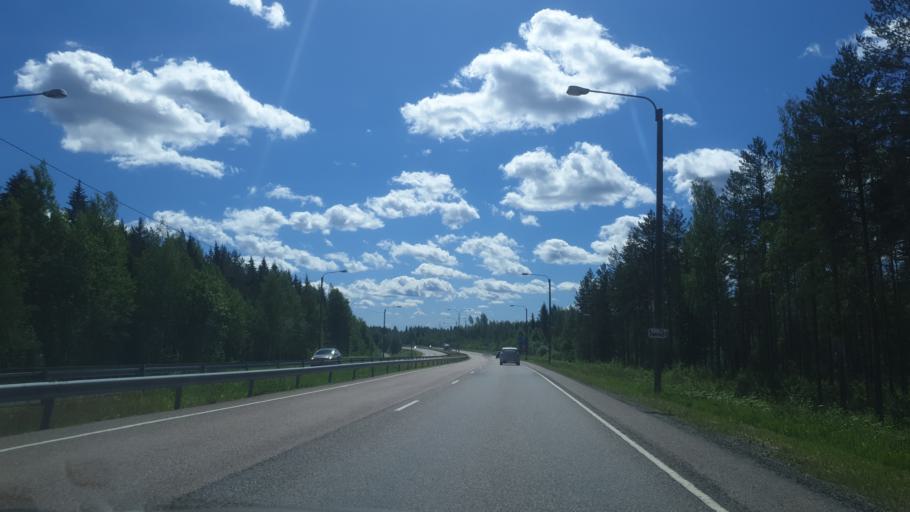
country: FI
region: Northern Savo
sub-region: Varkaus
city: Varkaus
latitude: 62.3411
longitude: 27.8210
